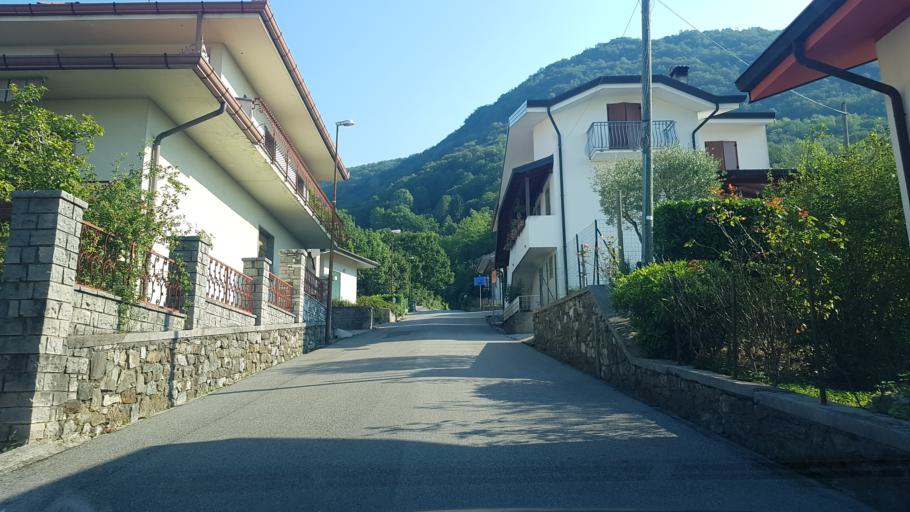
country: IT
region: Friuli Venezia Giulia
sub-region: Provincia di Udine
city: Nimis
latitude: 46.2233
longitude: 13.2473
